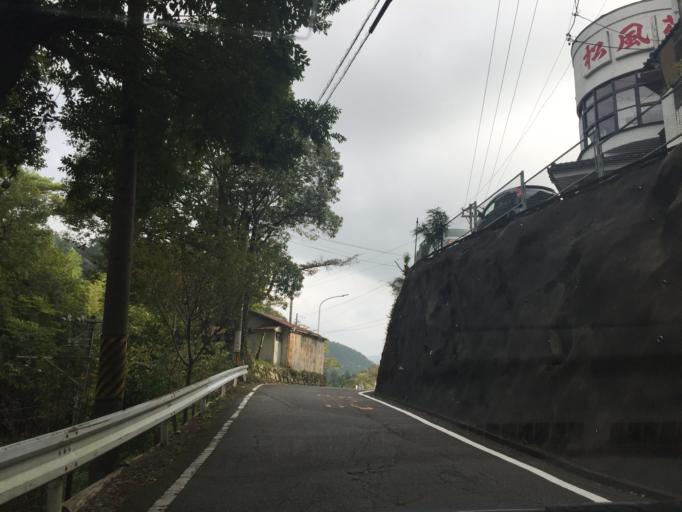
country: JP
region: Aichi
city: Shinshiro
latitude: 34.9689
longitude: 137.6128
